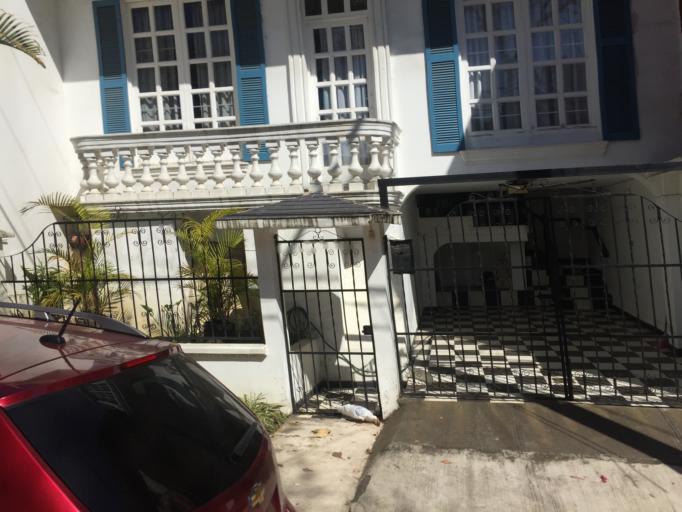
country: MX
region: Veracruz
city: El Castillo
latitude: 19.5331
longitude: -96.8881
